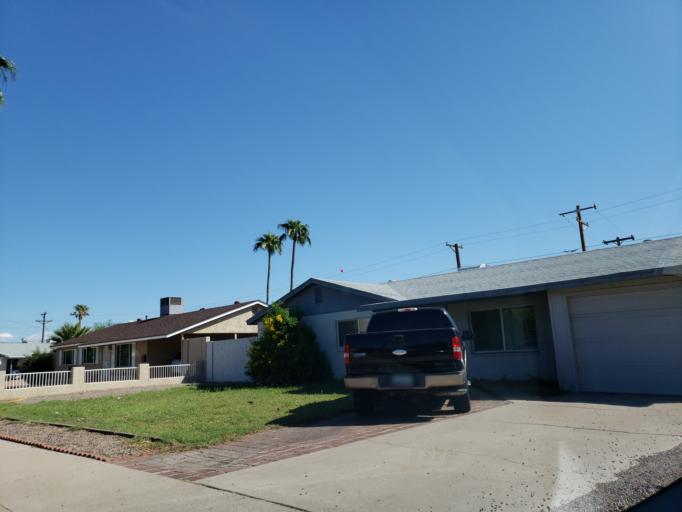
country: US
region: Arizona
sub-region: Maricopa County
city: Tempe Junction
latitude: 33.4630
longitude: -111.9348
